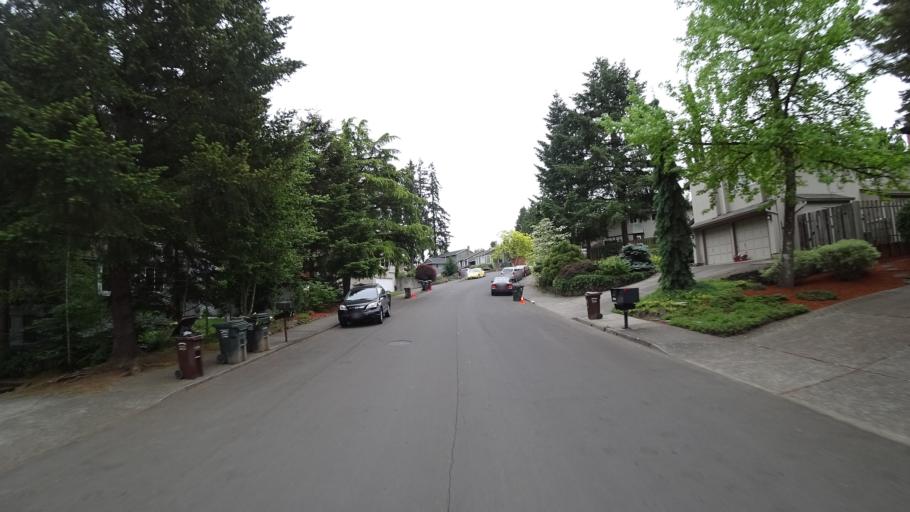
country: US
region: Oregon
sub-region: Washington County
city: Bethany
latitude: 45.5537
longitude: -122.8642
